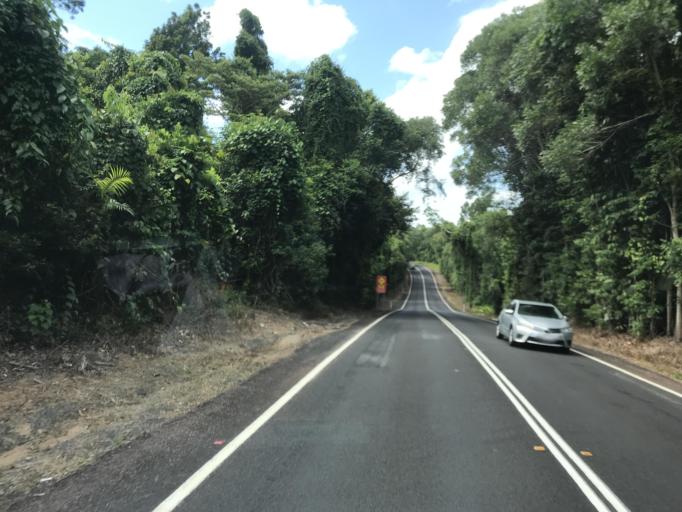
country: AU
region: Queensland
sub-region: Cassowary Coast
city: Innisfail
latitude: -17.8592
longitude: 146.0653
